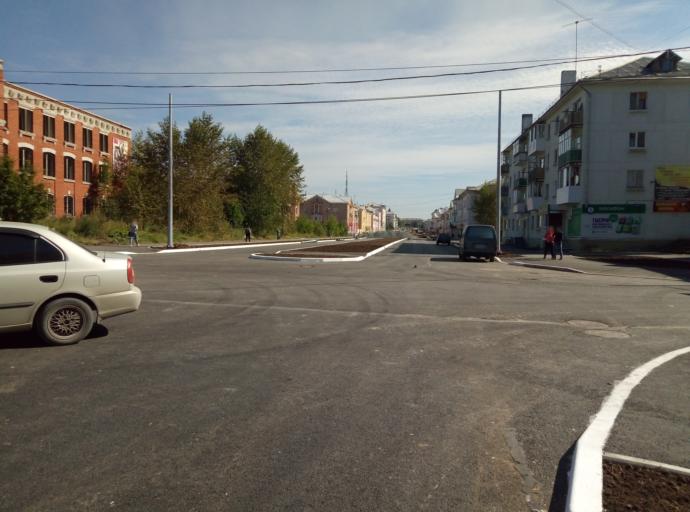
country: RU
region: Sverdlovsk
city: Krasnotur'insk
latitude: 59.7637
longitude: 60.1838
